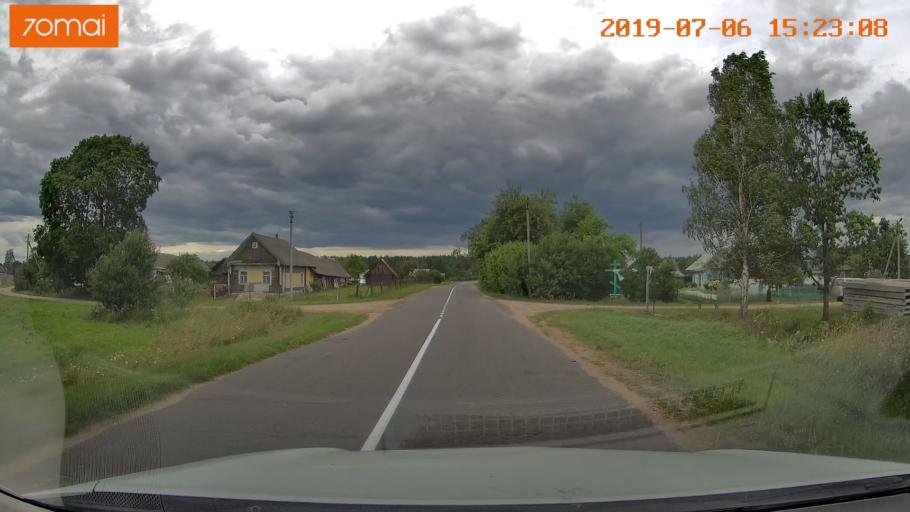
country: BY
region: Minsk
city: Valozhyn
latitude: 54.0162
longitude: 26.6045
